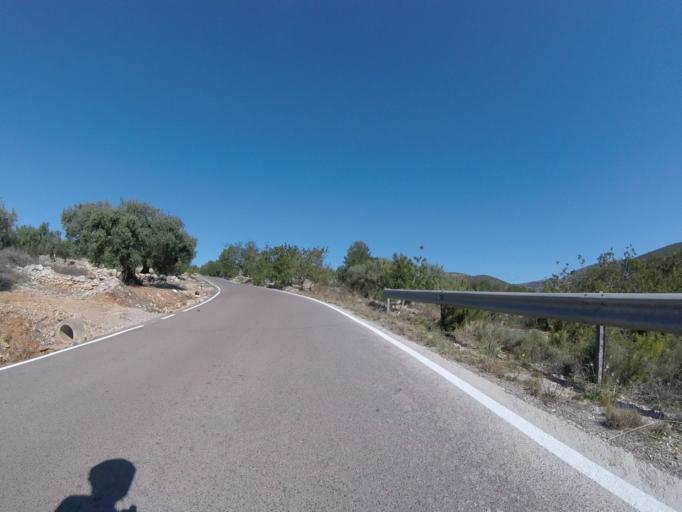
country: ES
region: Valencia
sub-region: Provincia de Castello
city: Santa Magdalena de Pulpis
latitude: 40.3736
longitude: 0.2724
